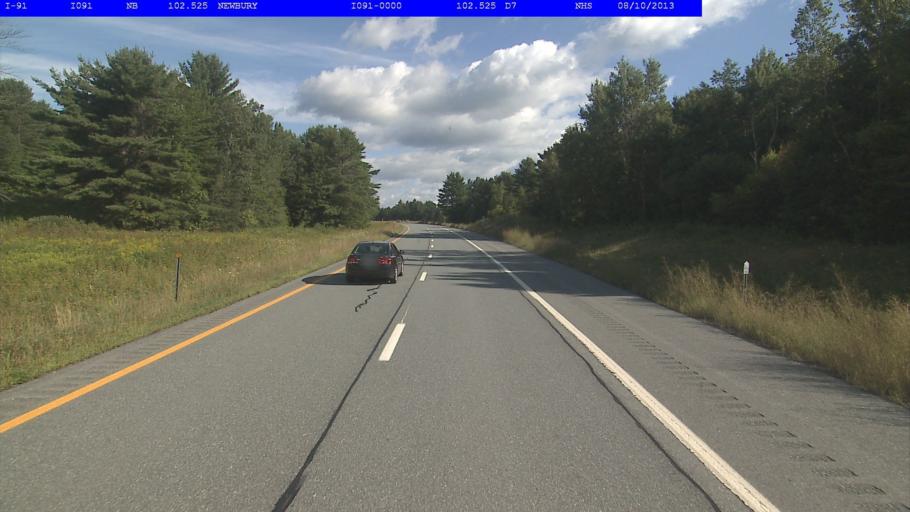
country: US
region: New Hampshire
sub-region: Grafton County
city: Haverhill
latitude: 44.0499
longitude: -72.1062
